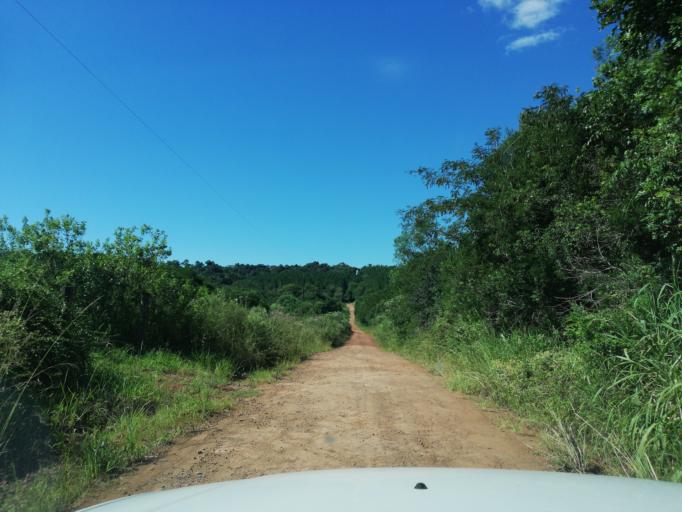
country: AR
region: Misiones
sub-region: Departamento de Leandro N. Alem
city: Leandro N. Alem
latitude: -27.5787
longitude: -55.3732
